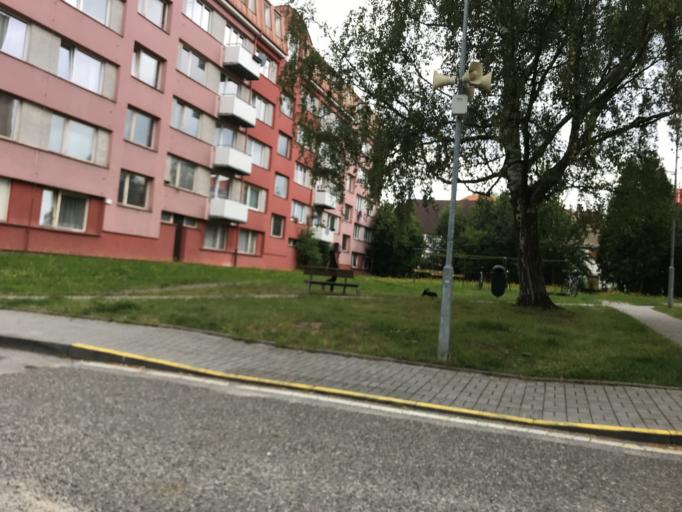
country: CZ
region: Jihocesky
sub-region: Okres Jindrichuv Hradec
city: Trebon
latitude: 49.0045
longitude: 14.7640
